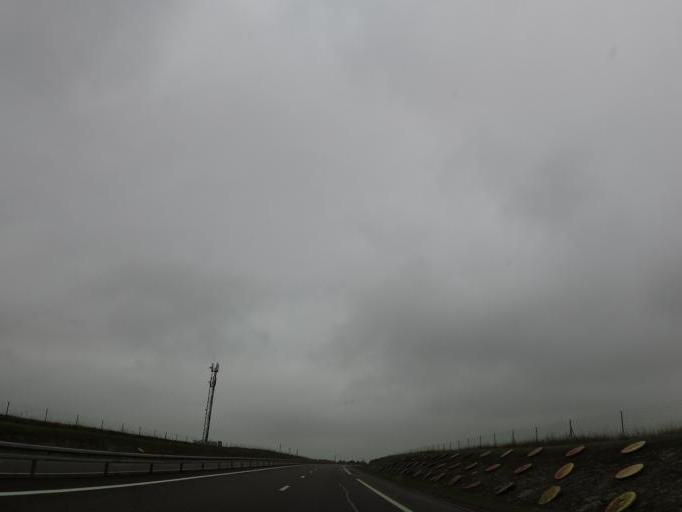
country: FR
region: Champagne-Ardenne
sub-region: Departement de la Marne
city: Courtisols
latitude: 49.0356
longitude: 4.5787
